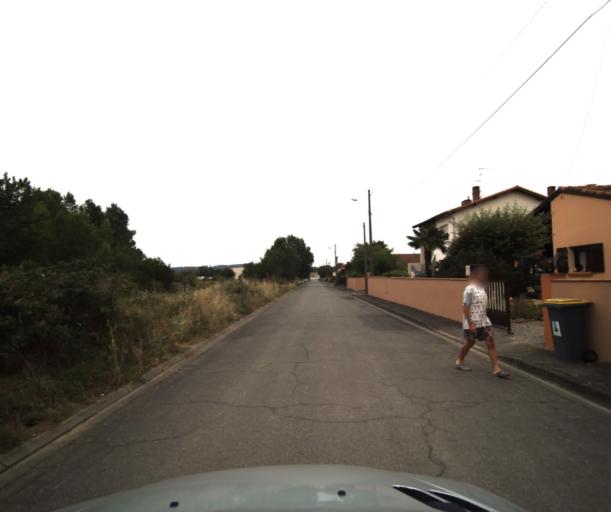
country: FR
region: Midi-Pyrenees
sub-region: Departement de la Haute-Garonne
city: Portet-sur-Garonne
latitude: 43.5452
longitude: 1.4071
